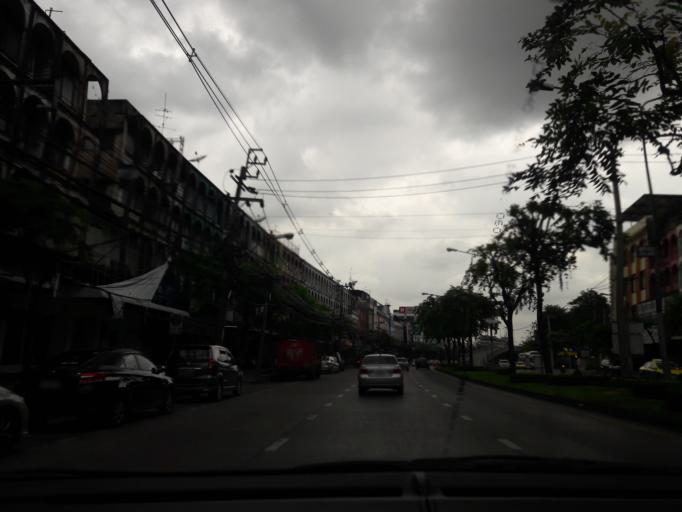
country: TH
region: Bangkok
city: Bangkok Noi
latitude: 13.7653
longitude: 100.4832
